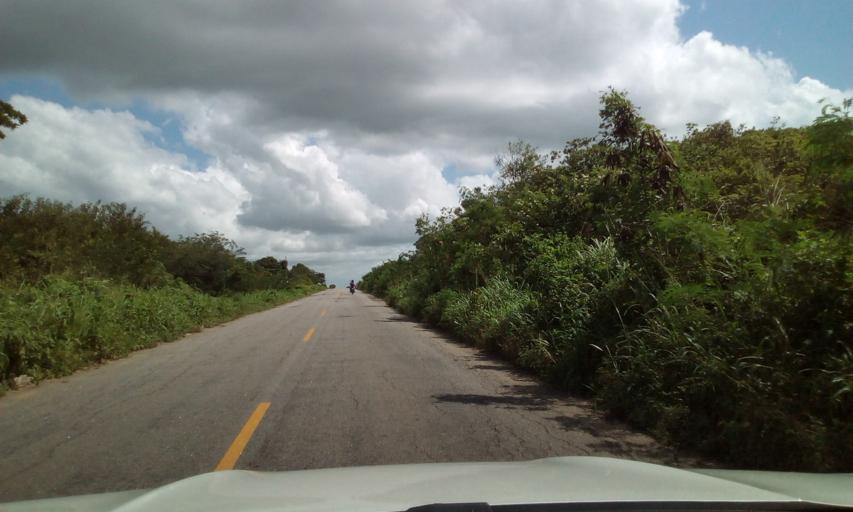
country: BR
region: Paraiba
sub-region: Guarabira
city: Guarabira
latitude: -6.8548
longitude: -35.4068
